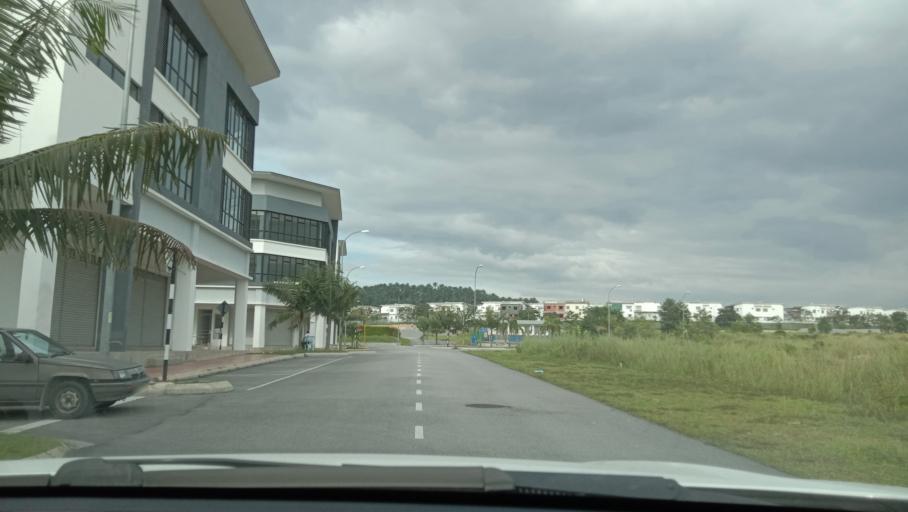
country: MY
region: Selangor
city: Ladang Seri Kundang
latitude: 3.2421
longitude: 101.4756
